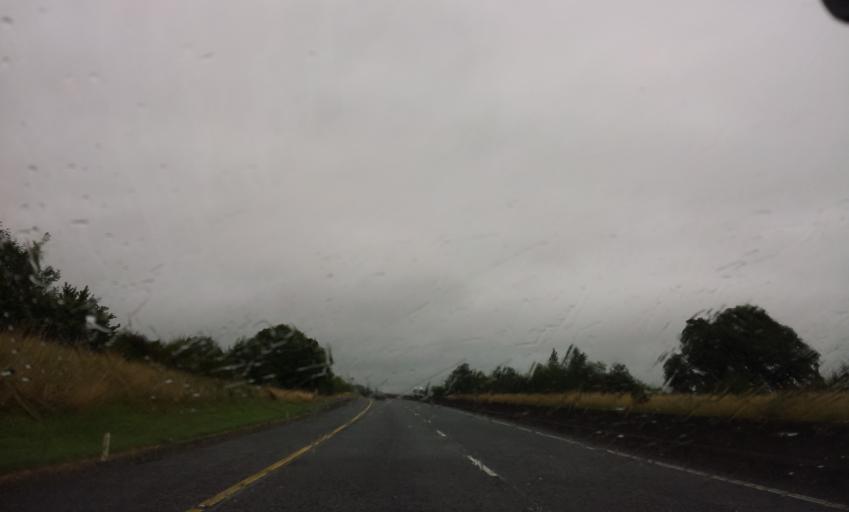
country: IE
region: Munster
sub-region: County Cork
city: Rathcormac
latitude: 52.0817
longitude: -8.2969
